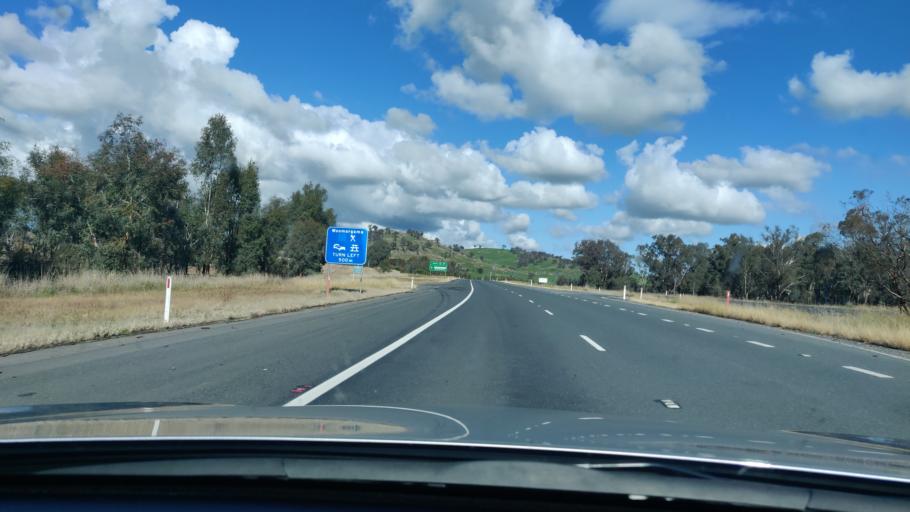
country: AU
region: New South Wales
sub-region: Greater Hume Shire
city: Holbrook
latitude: -35.7808
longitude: 147.2752
